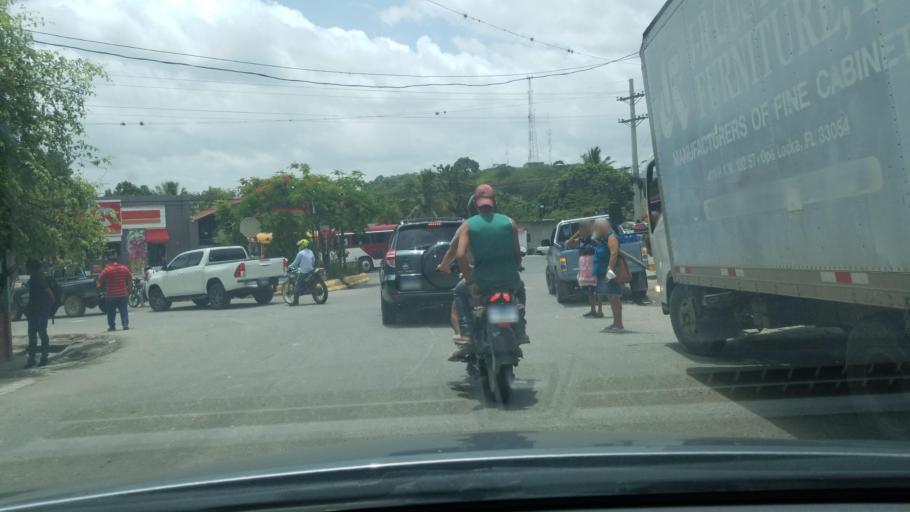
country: HN
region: Copan
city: Cucuyagua
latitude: 14.6510
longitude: -88.8766
